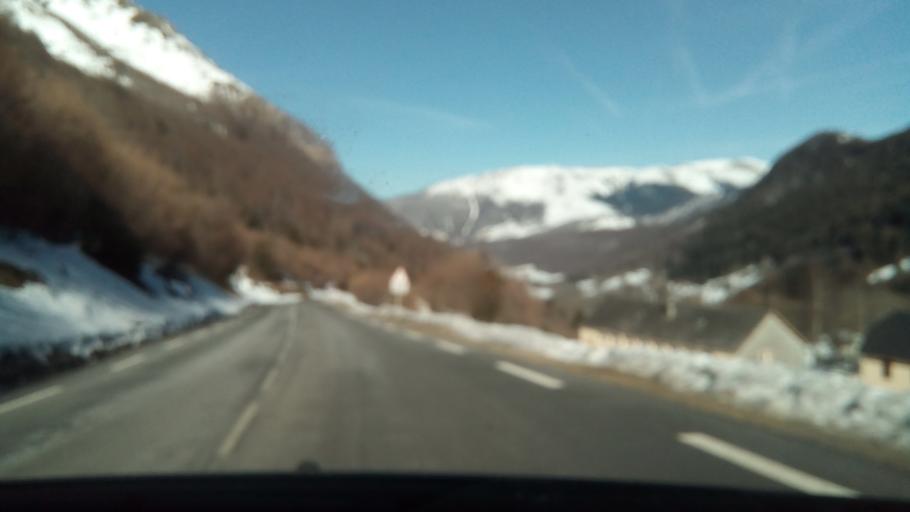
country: FR
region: Midi-Pyrenees
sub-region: Departement des Hautes-Pyrenees
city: Campan
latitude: 42.9312
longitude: 0.2040
